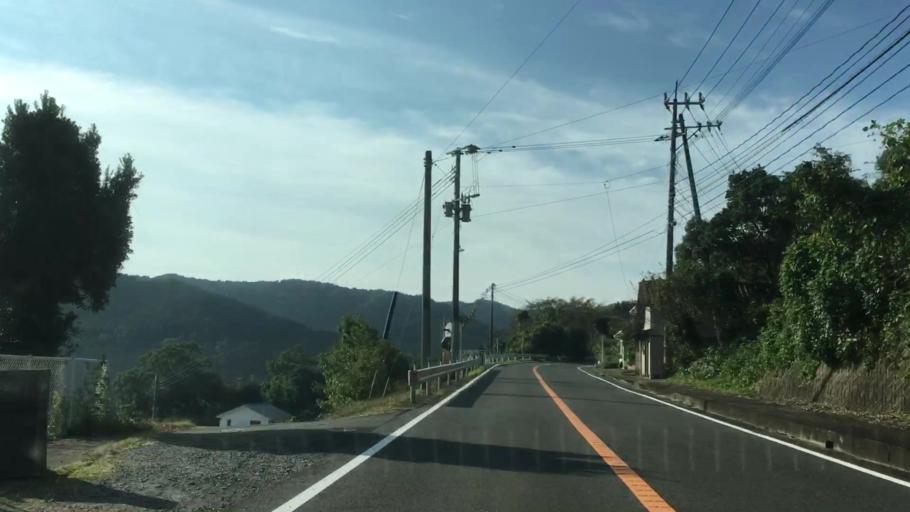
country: JP
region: Nagasaki
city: Sasebo
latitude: 32.9874
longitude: 129.7194
